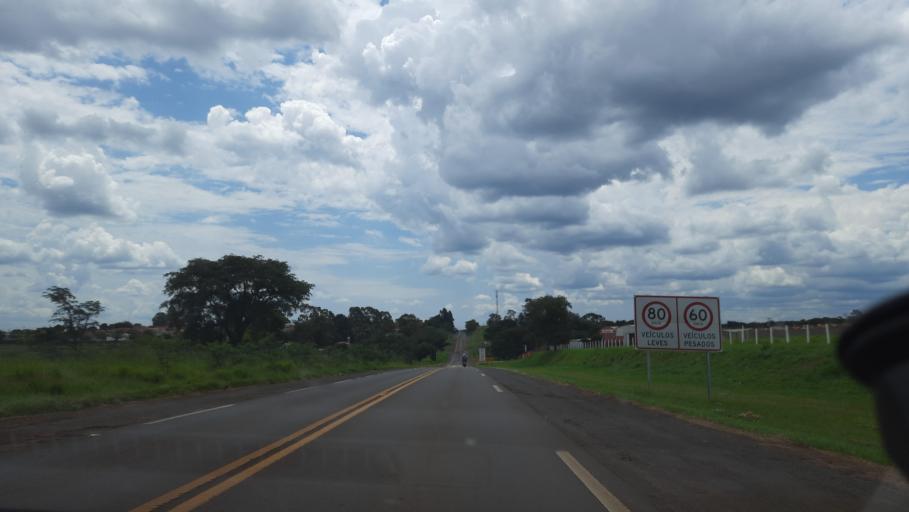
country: BR
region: Sao Paulo
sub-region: Cajuru
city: Cajuru
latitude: -21.2777
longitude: -47.2885
